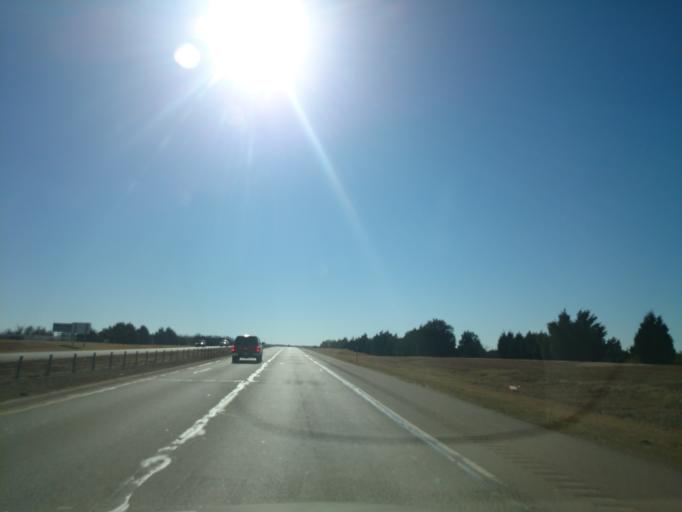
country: US
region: Oklahoma
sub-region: Logan County
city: Guthrie
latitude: 35.8533
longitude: -97.3944
